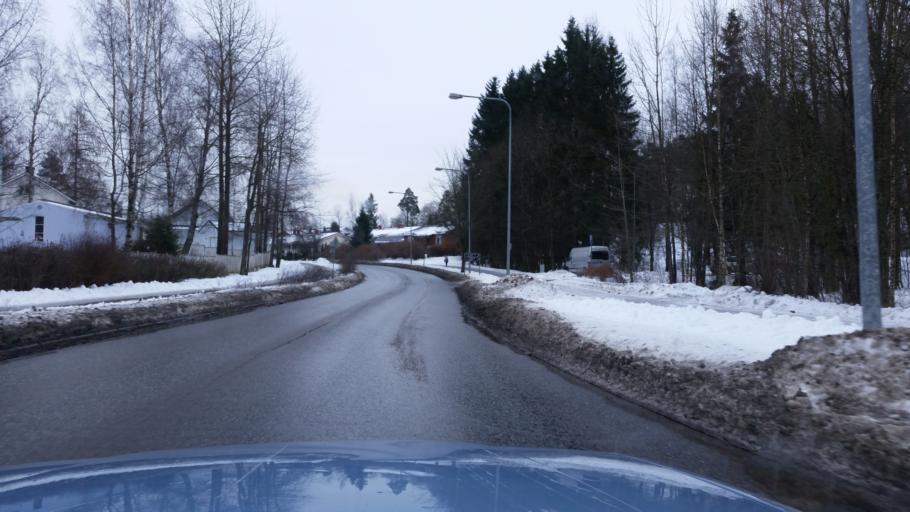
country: FI
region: Uusimaa
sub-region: Helsinki
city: Vantaa
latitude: 60.2707
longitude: 25.0533
